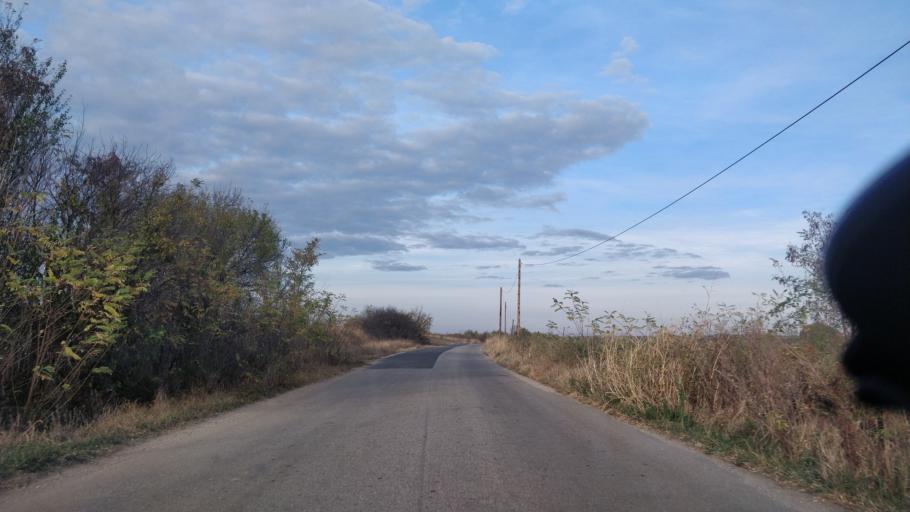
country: RO
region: Giurgiu
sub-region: Comuna Bucsani
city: Bucsani
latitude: 44.3556
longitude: 25.6587
